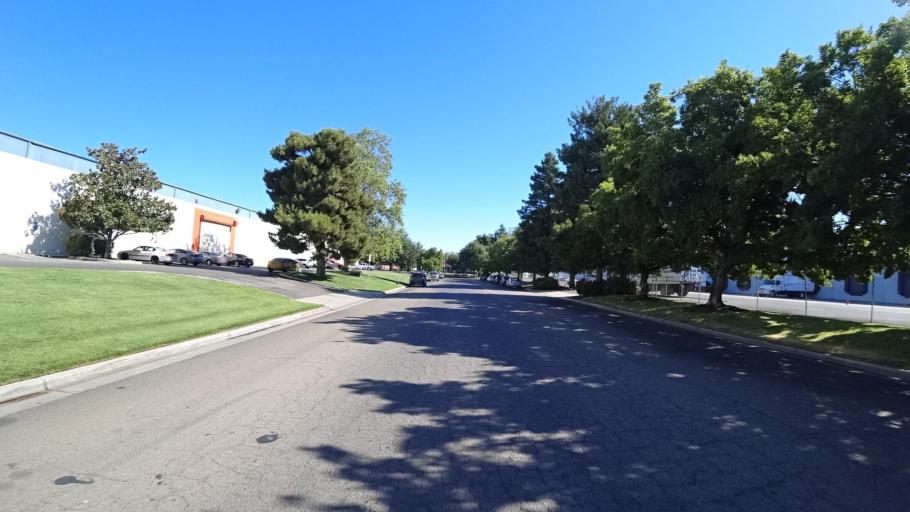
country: US
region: California
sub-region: Fresno County
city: Easton
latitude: 36.6955
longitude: -119.7765
